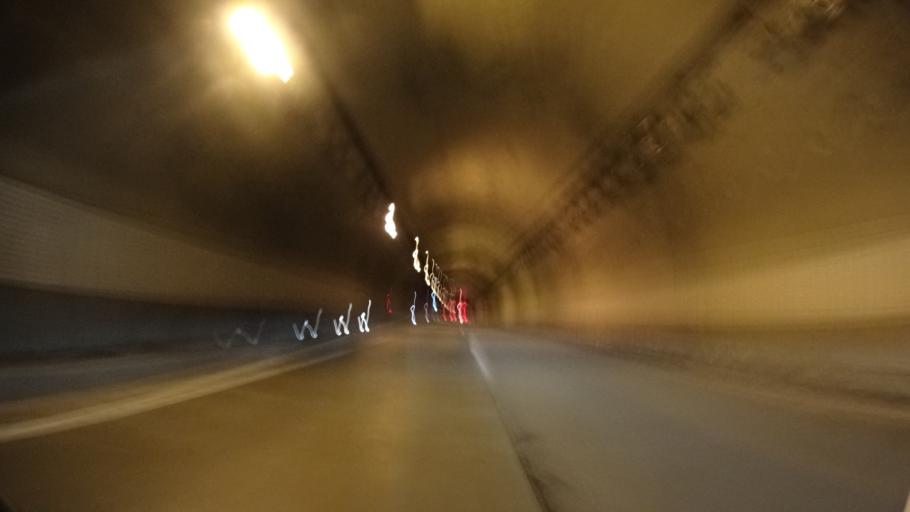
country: JP
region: Hyogo
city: Ono
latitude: 34.8415
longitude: 134.8568
